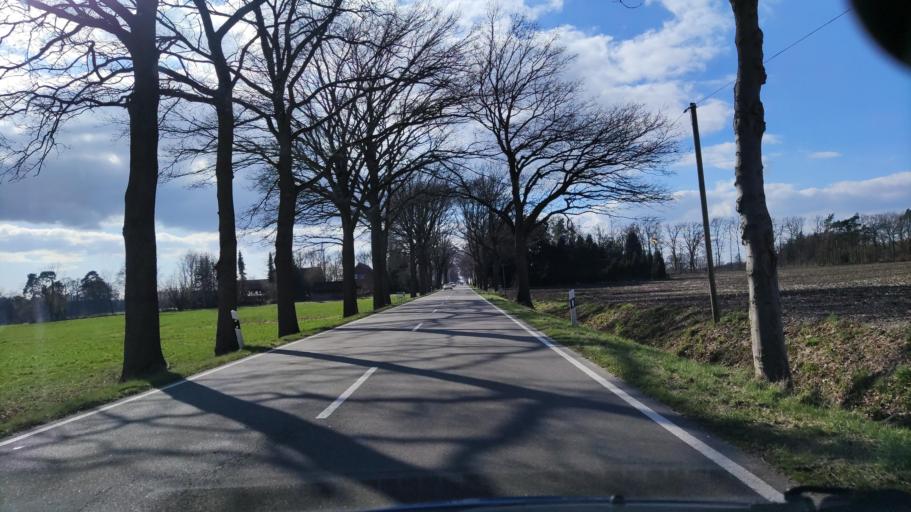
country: DE
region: Lower Saxony
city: Eldingen
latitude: 52.6676
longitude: 10.2986
